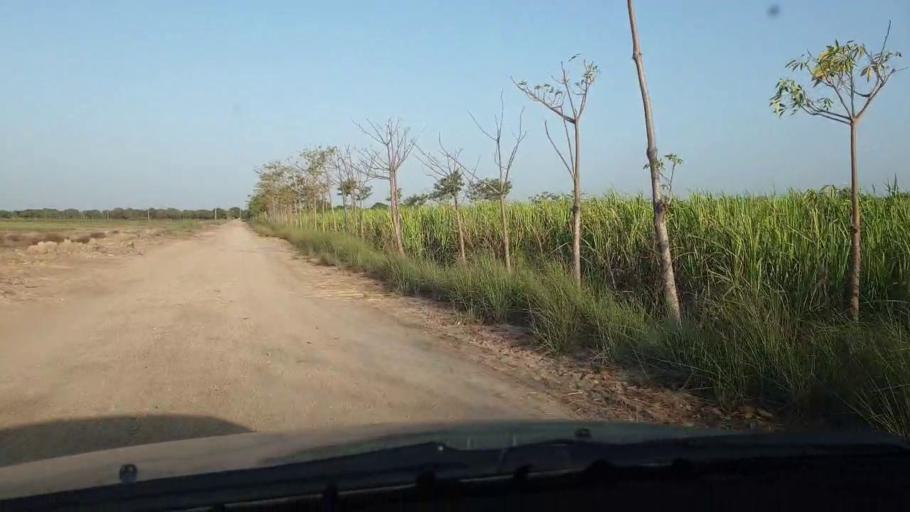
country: PK
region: Sindh
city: Mirwah Gorchani
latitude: 25.2735
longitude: 68.9398
